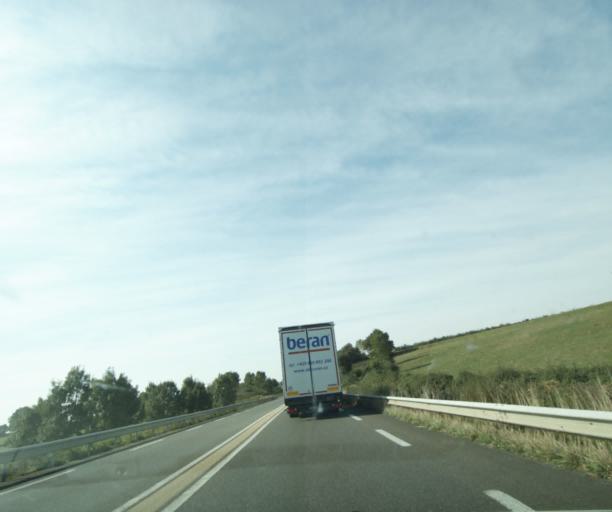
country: FR
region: Bourgogne
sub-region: Departement de Saone-et-Loire
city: Genelard
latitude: 46.5846
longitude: 4.2199
